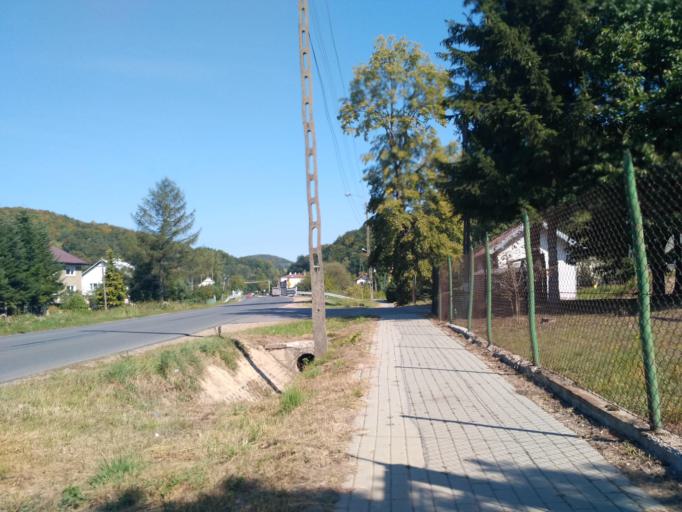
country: PL
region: Subcarpathian Voivodeship
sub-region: Powiat brzozowski
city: Grabownica Starzenska
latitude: 49.6646
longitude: 22.0824
